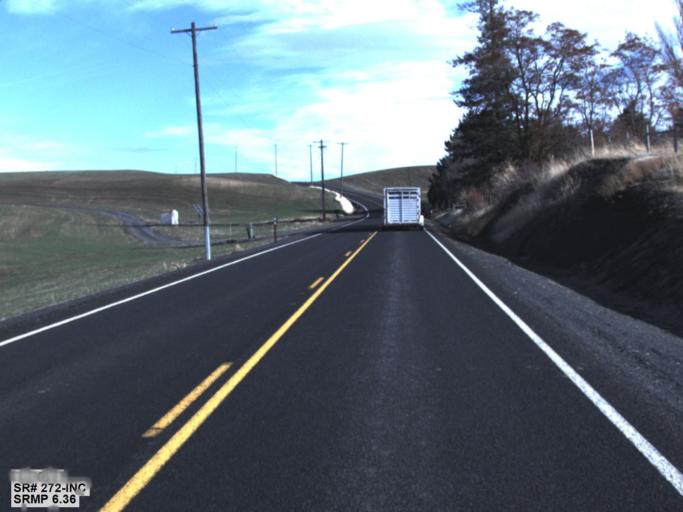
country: US
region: Washington
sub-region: Whitman County
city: Colfax
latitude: 46.9215
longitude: -117.2560
